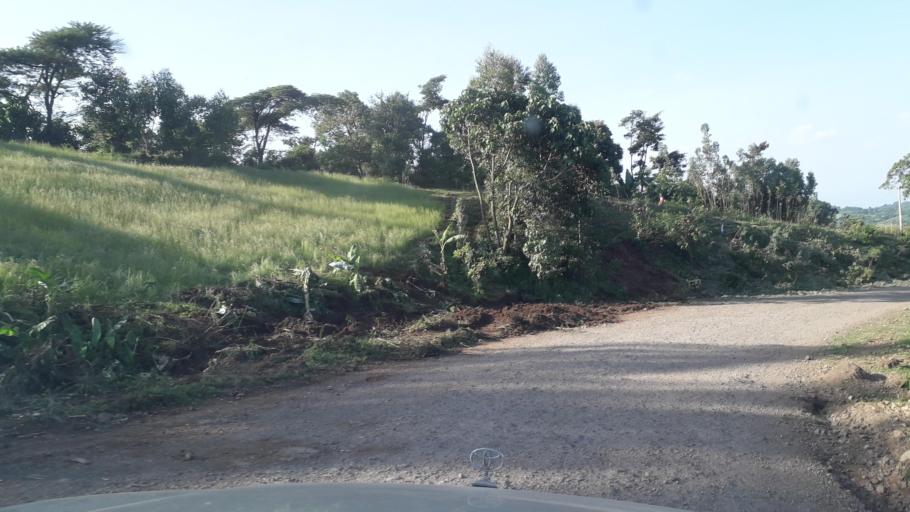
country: ET
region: Oromiya
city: Jima
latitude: 7.4688
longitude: 36.8754
